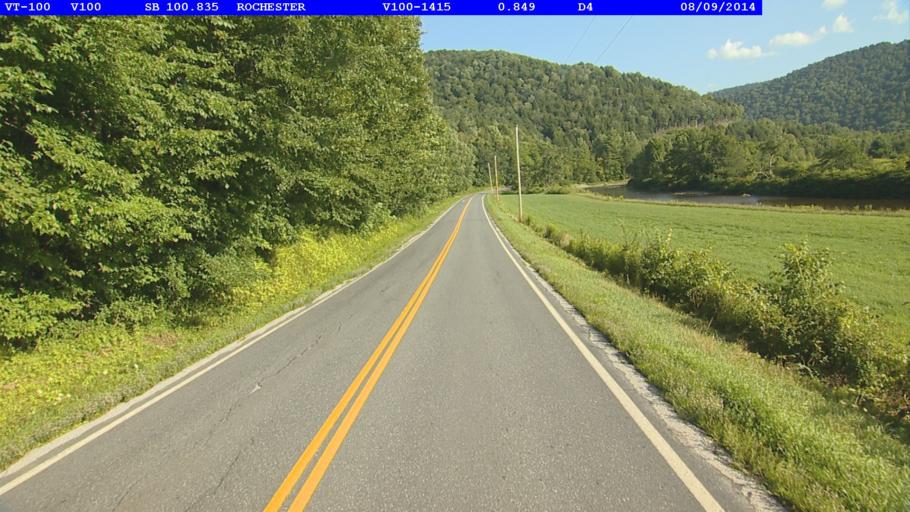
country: US
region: Vermont
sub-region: Orange County
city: Randolph
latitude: 43.8159
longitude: -72.7857
